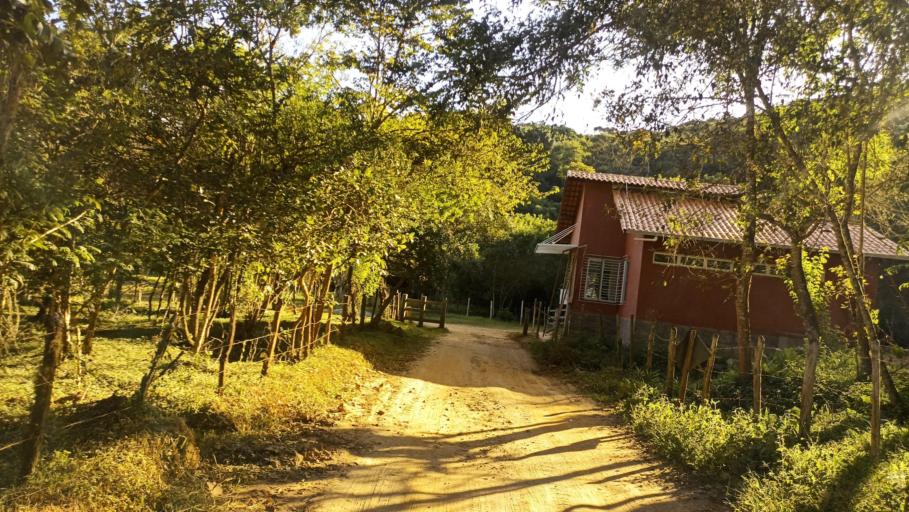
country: BR
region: Minas Gerais
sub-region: Ouro Preto
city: Ouro Preto
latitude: -20.2971
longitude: -43.5742
